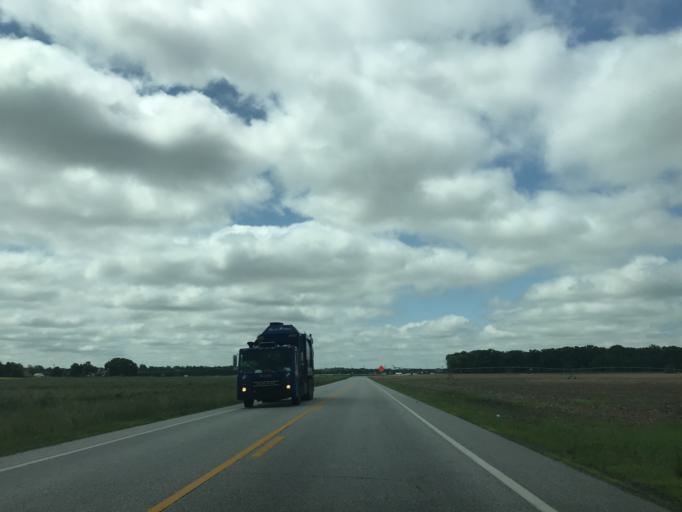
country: US
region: Maryland
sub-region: Caroline County
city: Ridgely
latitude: 38.9208
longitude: -75.8926
